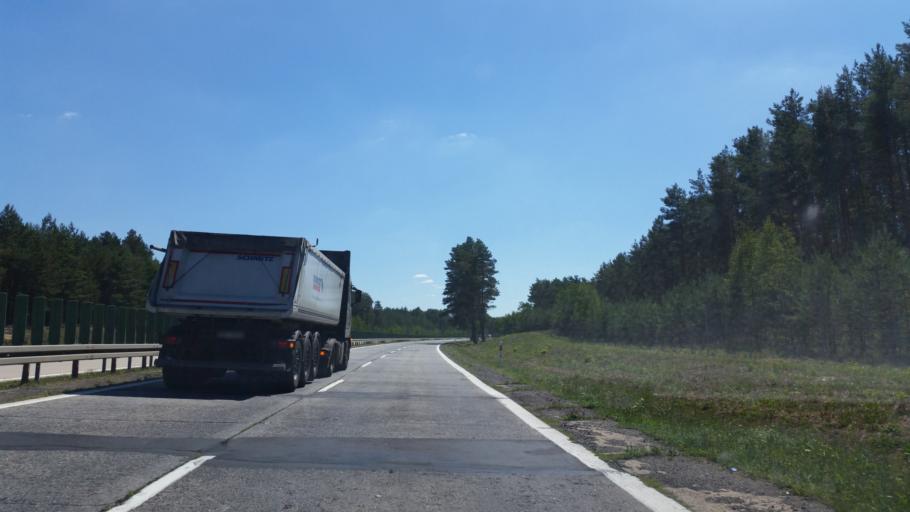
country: PL
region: Lubusz
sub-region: Powiat zaganski
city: Ilowa
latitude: 51.5178
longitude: 15.2311
